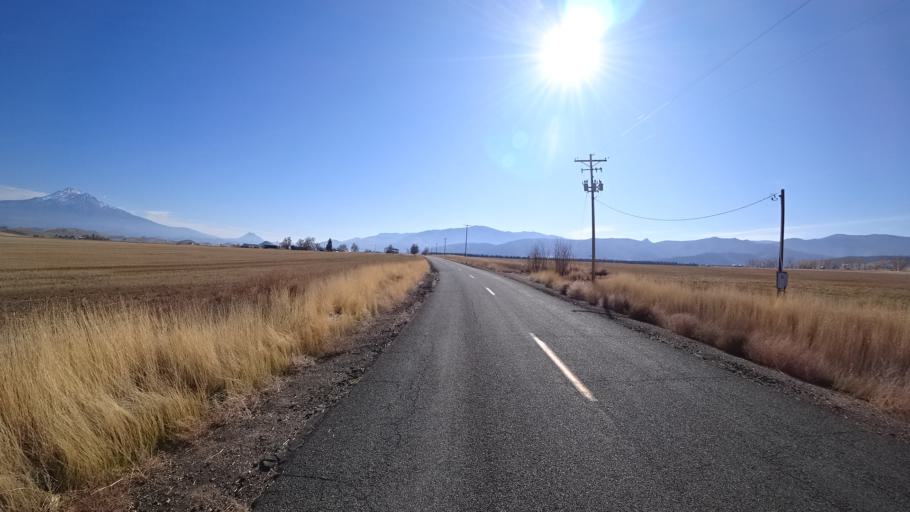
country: US
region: California
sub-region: Siskiyou County
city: Montague
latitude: 41.5635
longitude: -122.5480
